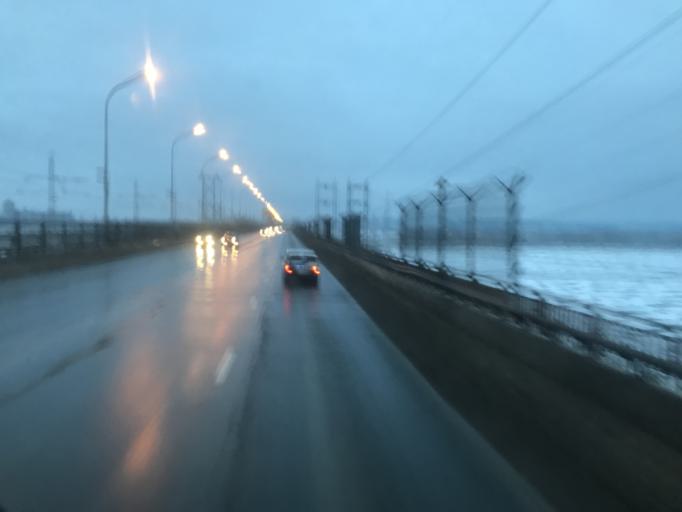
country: RU
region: Samara
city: Zhigulevsk
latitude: 53.4554
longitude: 49.4951
